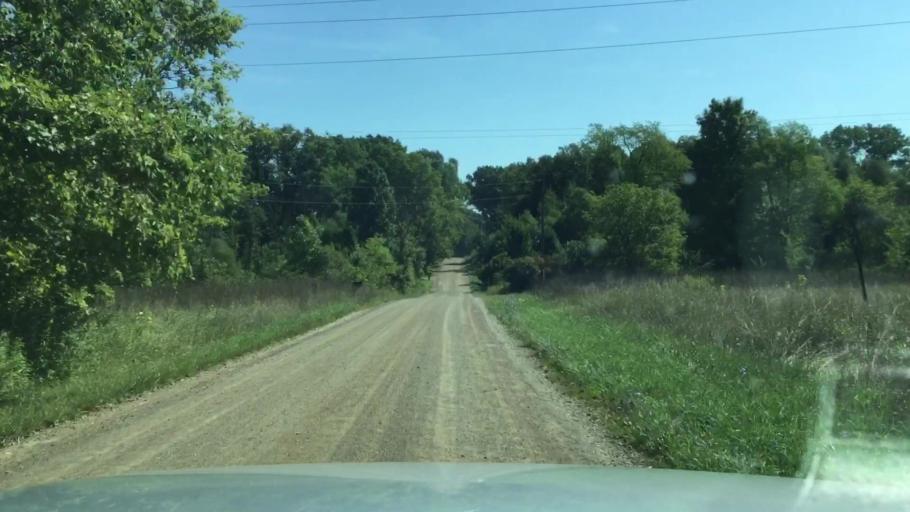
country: US
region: Michigan
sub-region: Lenawee County
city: Manitou Beach-Devils Lake
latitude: 41.9936
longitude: -84.3300
